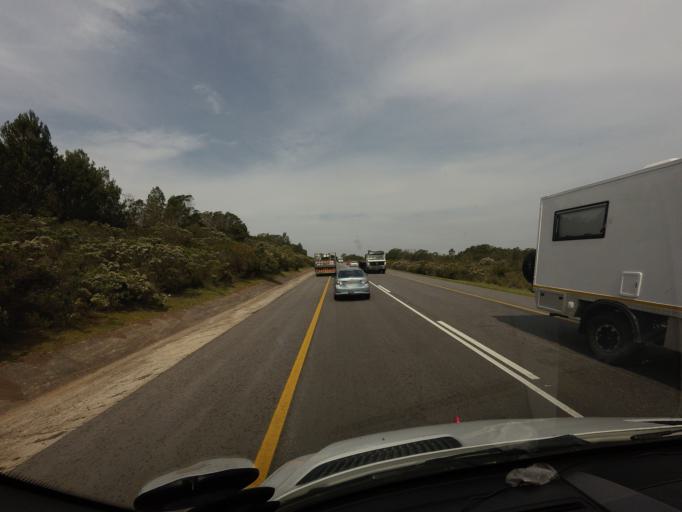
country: ZA
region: Eastern Cape
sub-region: Cacadu District Municipality
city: Kruisfontein
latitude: -33.9948
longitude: 24.7052
